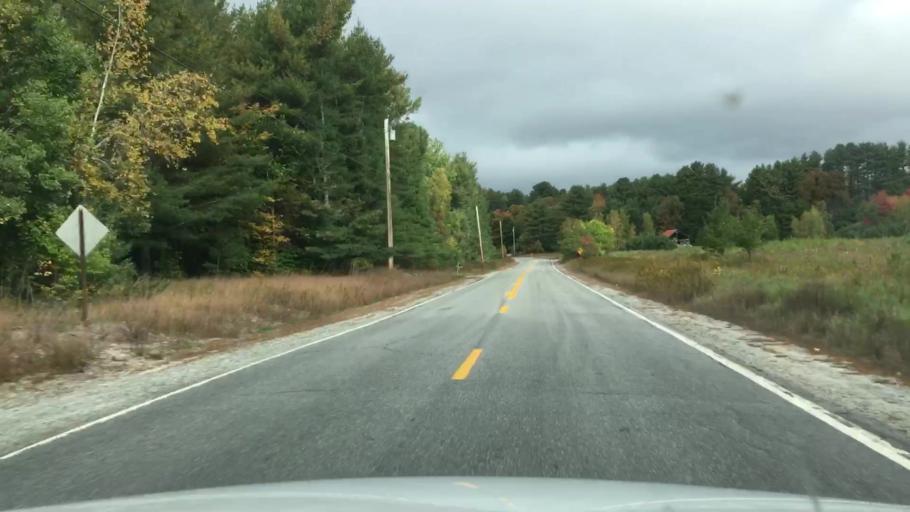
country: US
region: Maine
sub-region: Oxford County
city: Bethel
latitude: 44.3368
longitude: -70.7796
